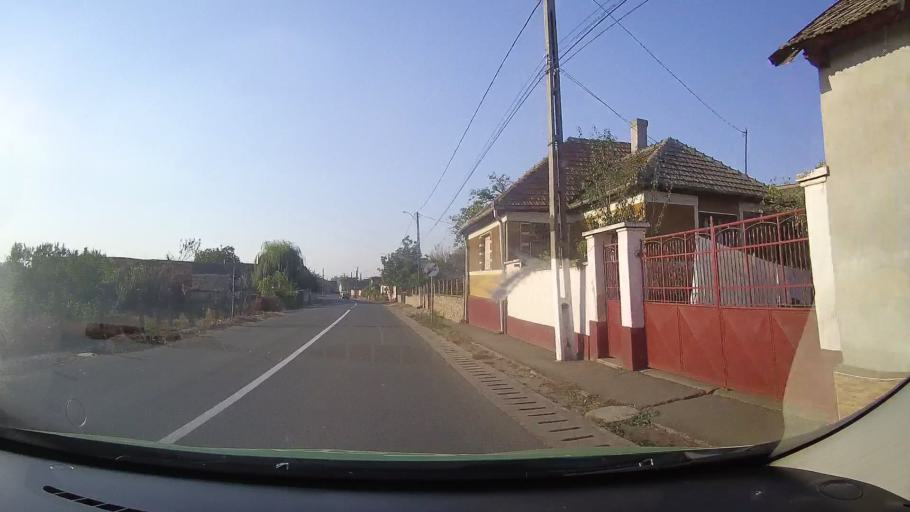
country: RO
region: Arad
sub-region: Comuna Covasint
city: Covasint
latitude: 46.2075
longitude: 21.6096
